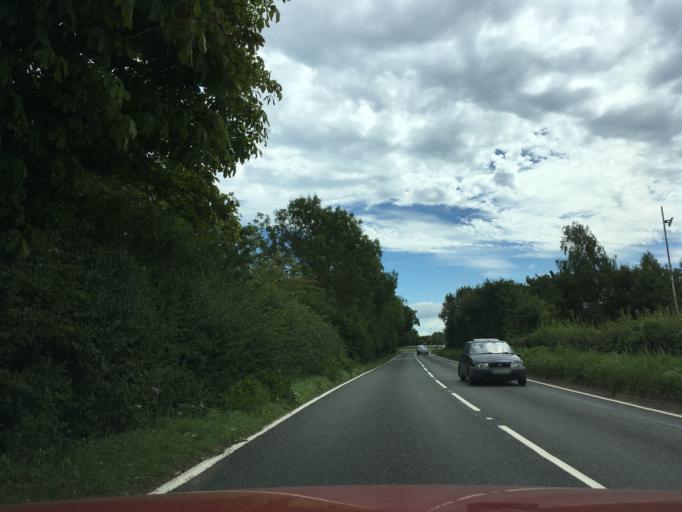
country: GB
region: England
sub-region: Somerset
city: Cheddar
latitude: 51.2716
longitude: -2.7733
